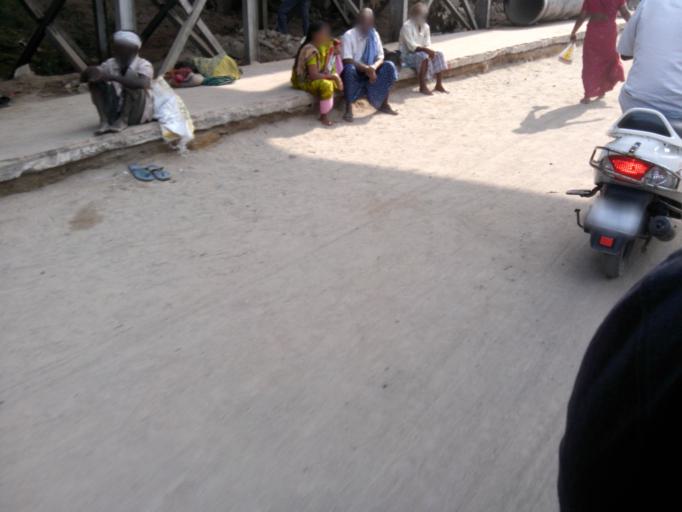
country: IN
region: Andhra Pradesh
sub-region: Krishna
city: Vijayawada
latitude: 16.5128
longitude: 80.6045
